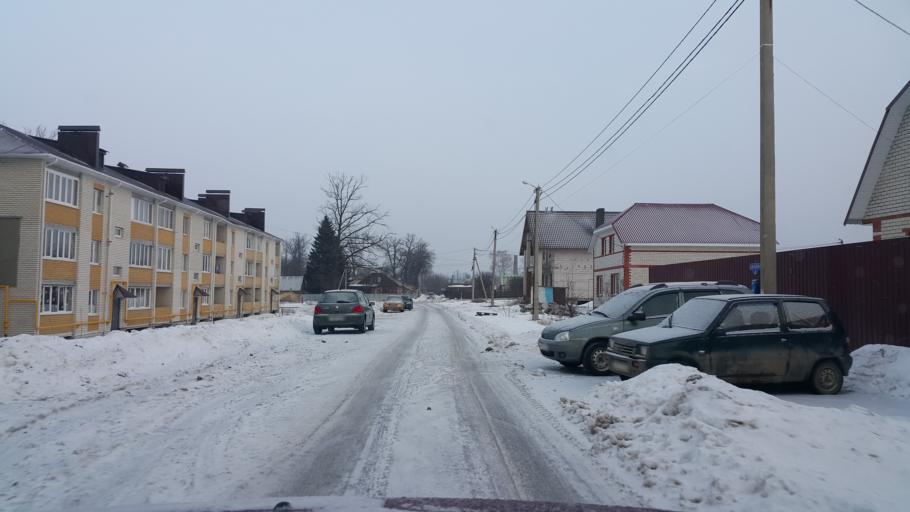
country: RU
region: Tambov
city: Kotovsk
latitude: 52.5753
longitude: 41.5218
